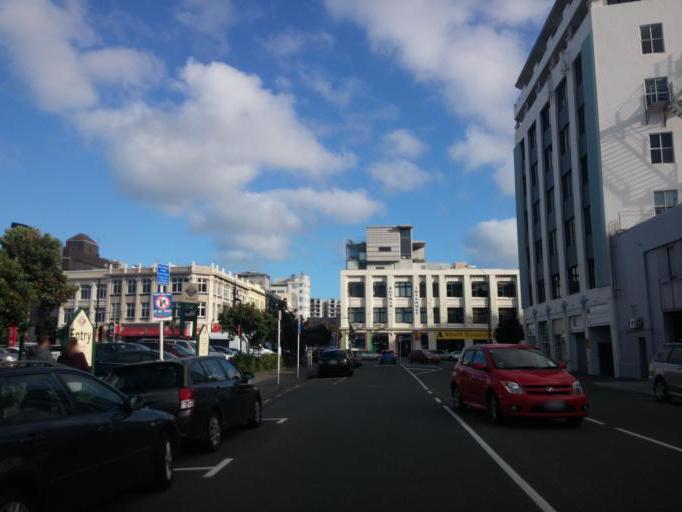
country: NZ
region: Wellington
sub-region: Wellington City
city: Wellington
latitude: -41.2920
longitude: 174.7836
